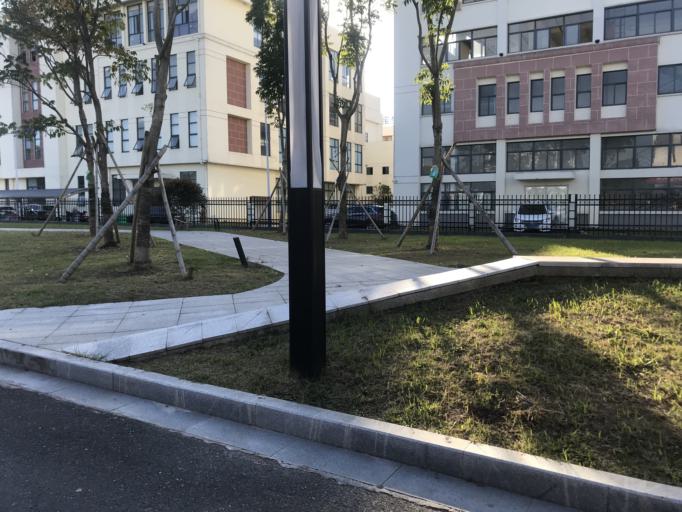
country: CN
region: Anhui Sheng
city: Xintan
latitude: 29.7720
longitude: 118.2587
